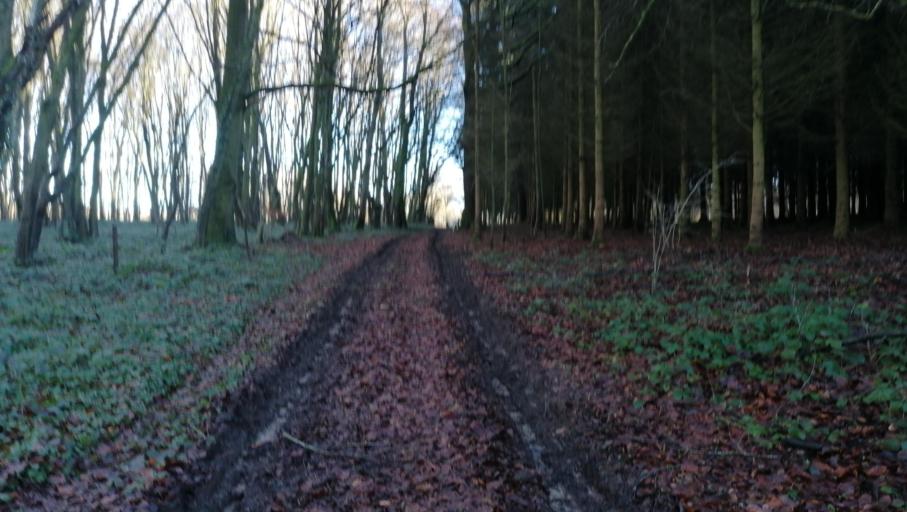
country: FR
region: Nord-Pas-de-Calais
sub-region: Departement du Nord
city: Recquignies
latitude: 50.2107
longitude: 4.0547
